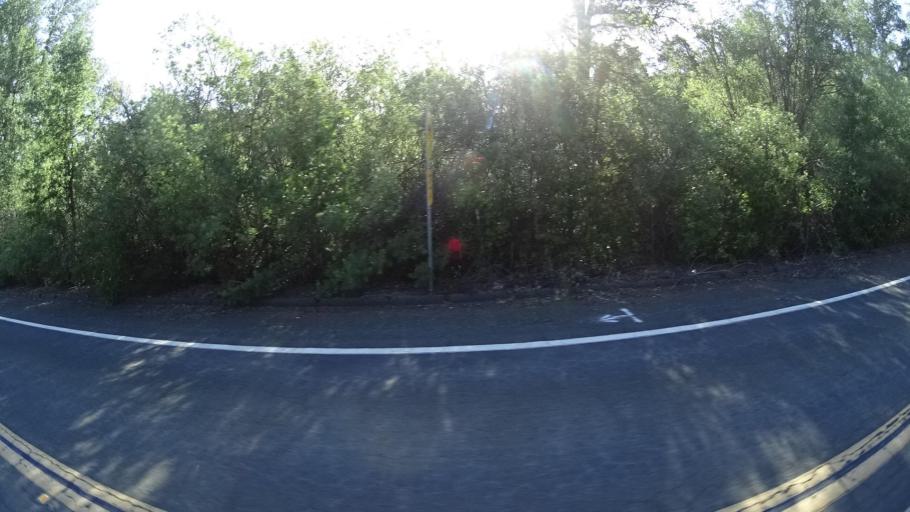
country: US
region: California
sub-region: Lake County
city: North Lakeport
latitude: 39.1094
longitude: -122.9755
